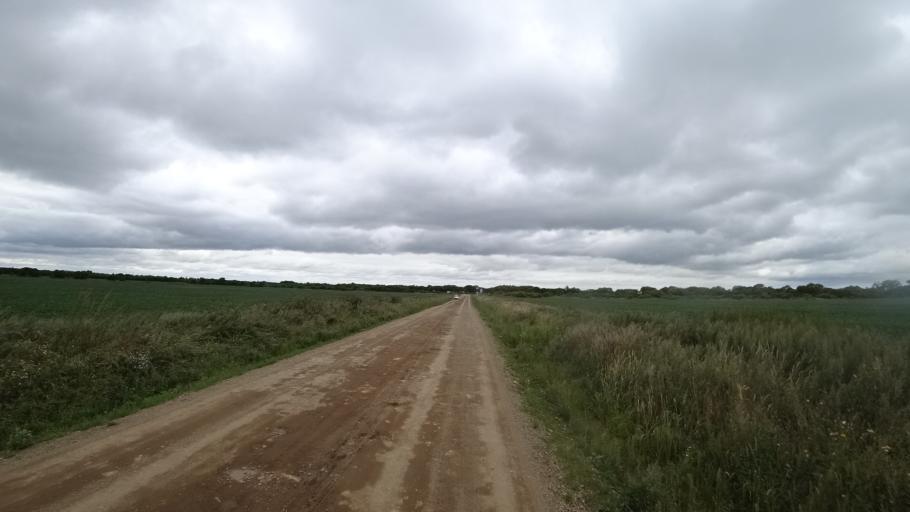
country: RU
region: Primorskiy
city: Chernigovka
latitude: 44.3440
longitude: 132.6105
